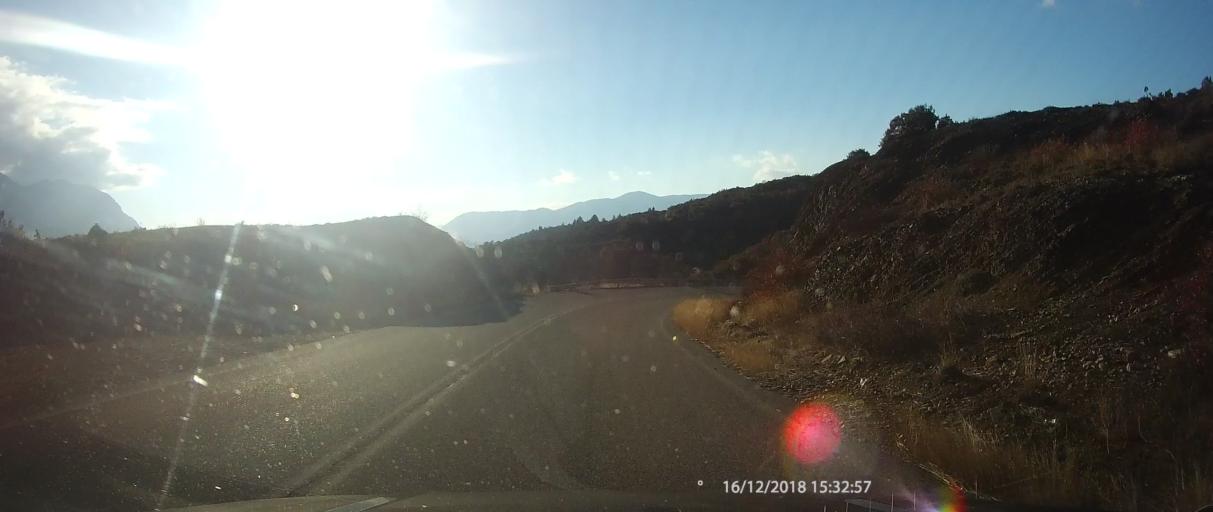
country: GR
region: Epirus
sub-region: Nomos Ioanninon
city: Konitsa
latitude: 40.0663
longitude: 20.7388
